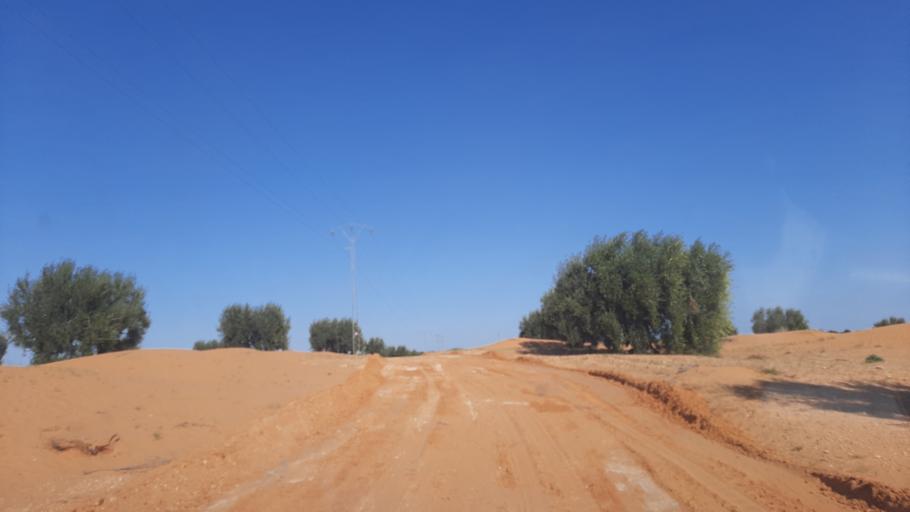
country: TN
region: Madanin
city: Medenine
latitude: 33.2835
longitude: 10.7843
